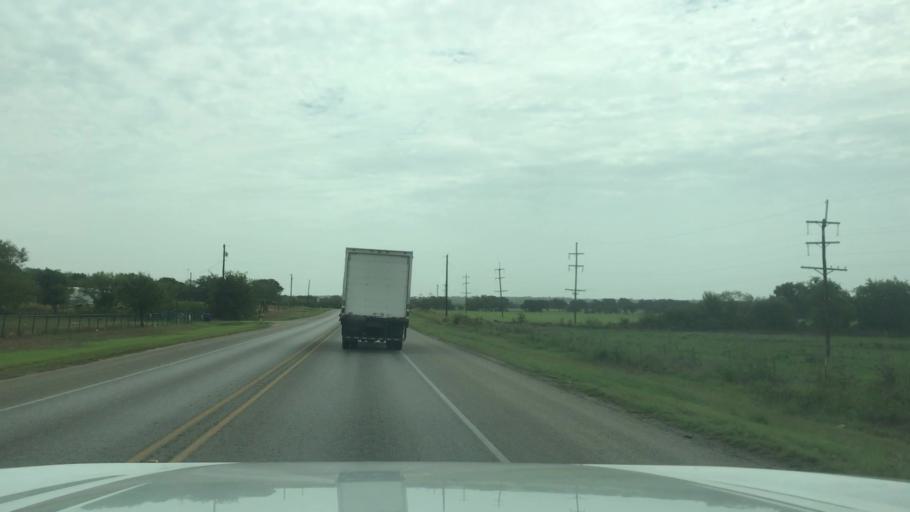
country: US
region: Texas
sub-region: Comanche County
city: De Leon
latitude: 32.0994
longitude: -98.4703
